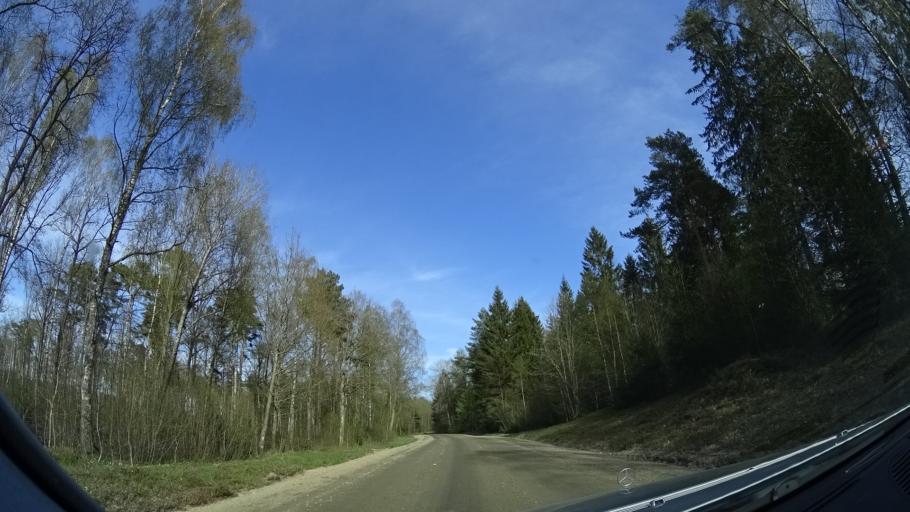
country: SE
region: Skane
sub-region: Hassleholms Kommun
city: Sosdala
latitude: 56.0865
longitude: 13.6847
